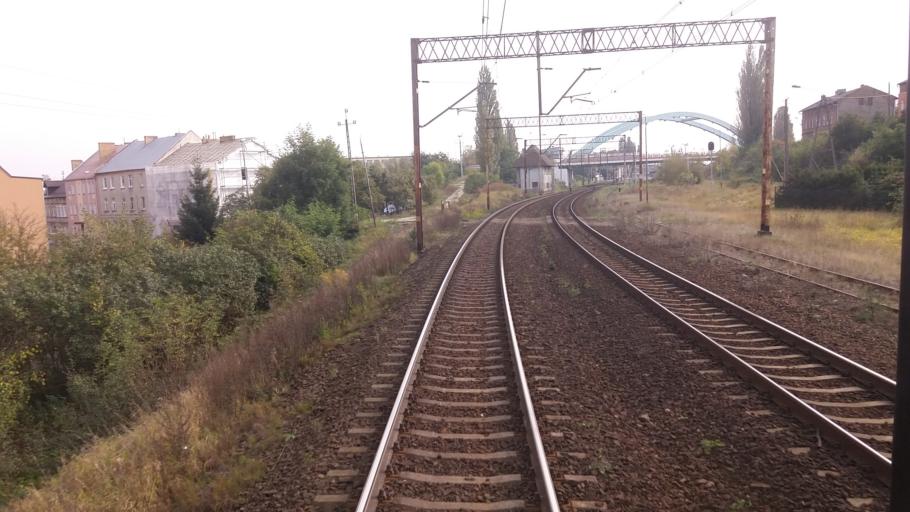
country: PL
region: West Pomeranian Voivodeship
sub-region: Powiat choszczenski
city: Choszczno
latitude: 53.1675
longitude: 15.3982
